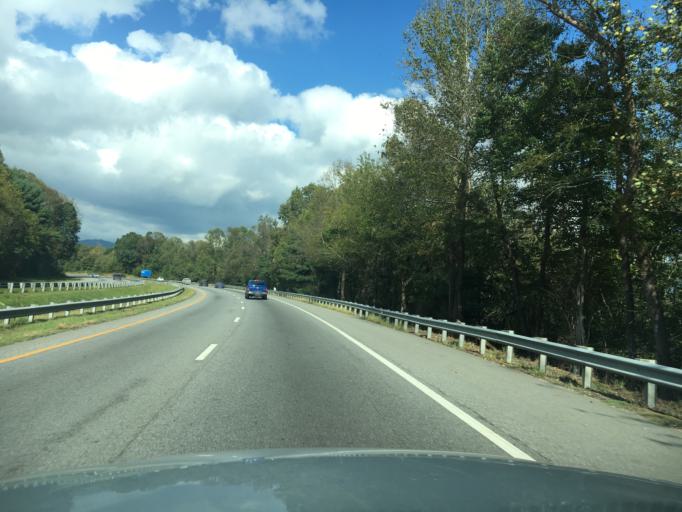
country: US
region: North Carolina
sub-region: Buncombe County
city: Asheville
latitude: 35.5627
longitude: -82.5730
